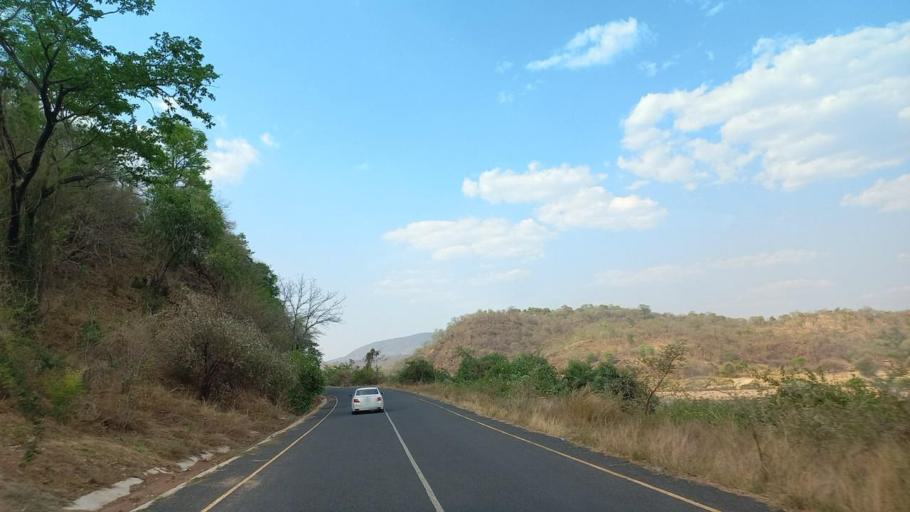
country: ZM
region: Lusaka
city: Luangwa
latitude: -15.0037
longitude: 30.2155
